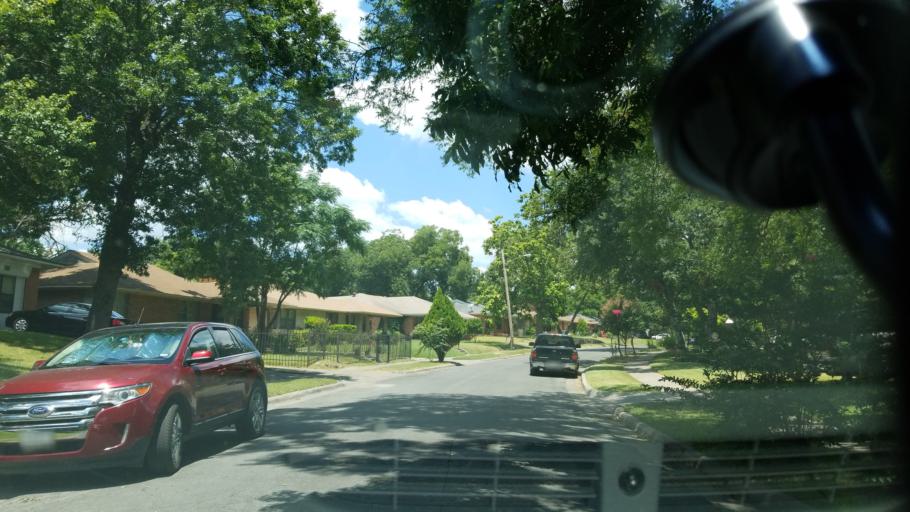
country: US
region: Texas
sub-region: Dallas County
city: Cockrell Hill
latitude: 32.7072
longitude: -96.8461
